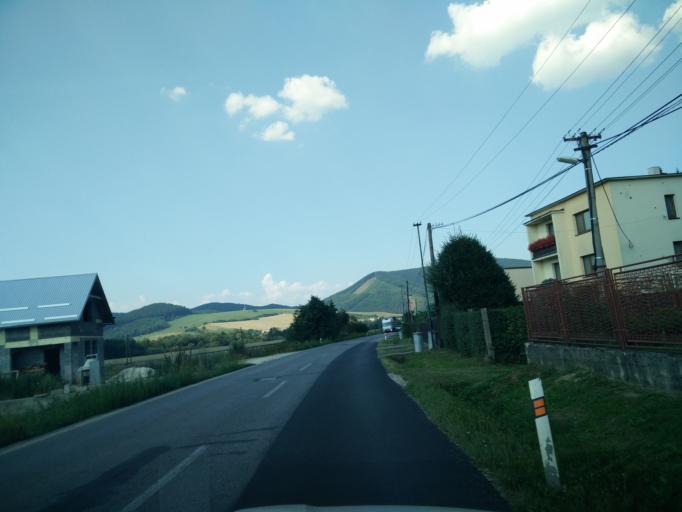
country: SK
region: Zilinsky
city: Rajec
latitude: 49.1096
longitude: 18.6469
